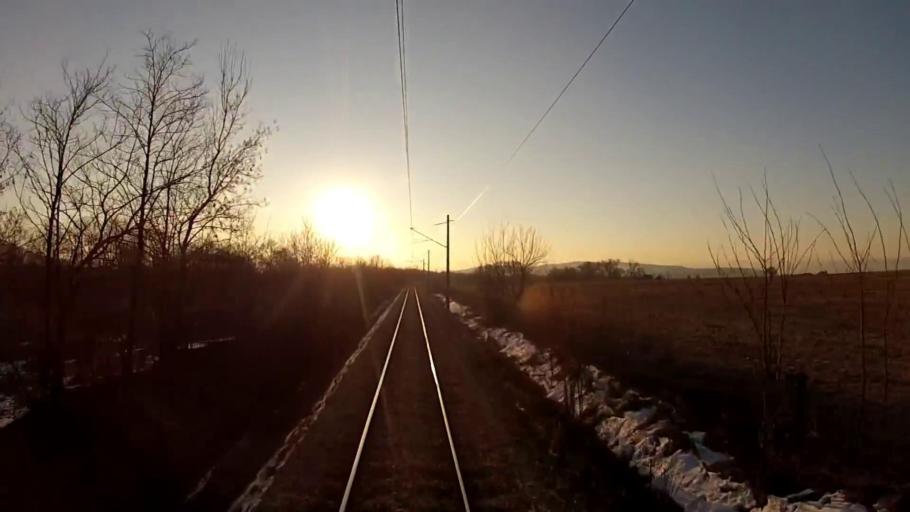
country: BG
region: Sofiya
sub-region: Obshtina Dragoman
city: Dragoman
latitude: 42.8863
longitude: 22.9789
